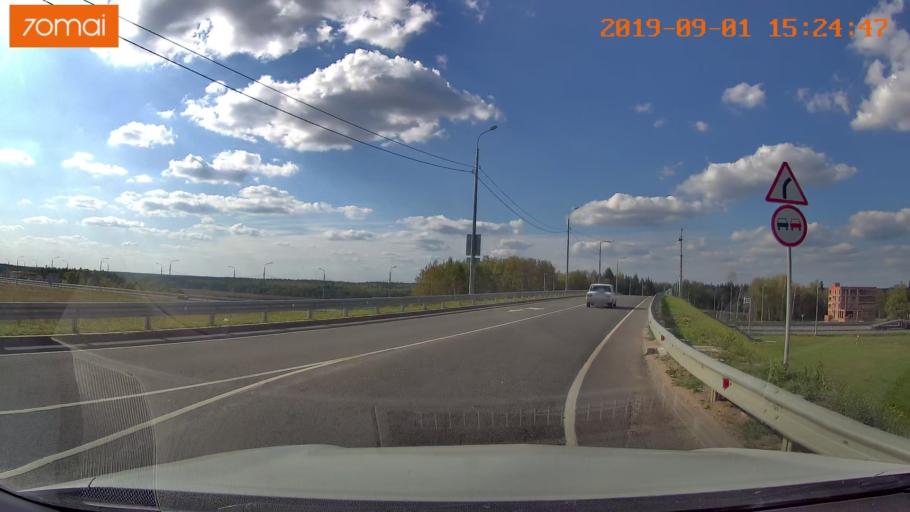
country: RU
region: Kaluga
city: Maloyaroslavets
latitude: 54.9560
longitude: 36.4574
